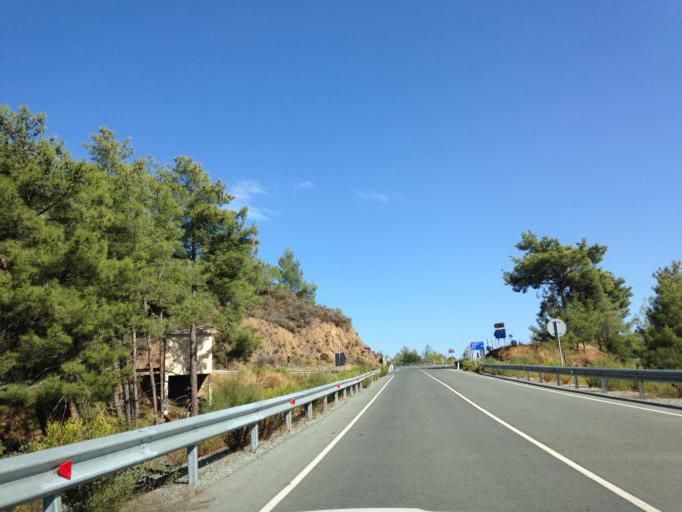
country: CY
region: Limassol
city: Pachna
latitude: 34.8692
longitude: 32.8252
